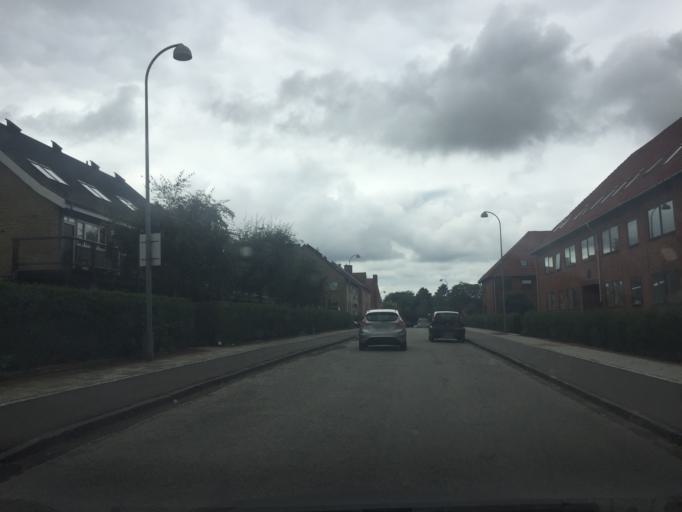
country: DK
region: Capital Region
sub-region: Gladsaxe Municipality
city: Buddinge
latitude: 55.7625
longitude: 12.4570
